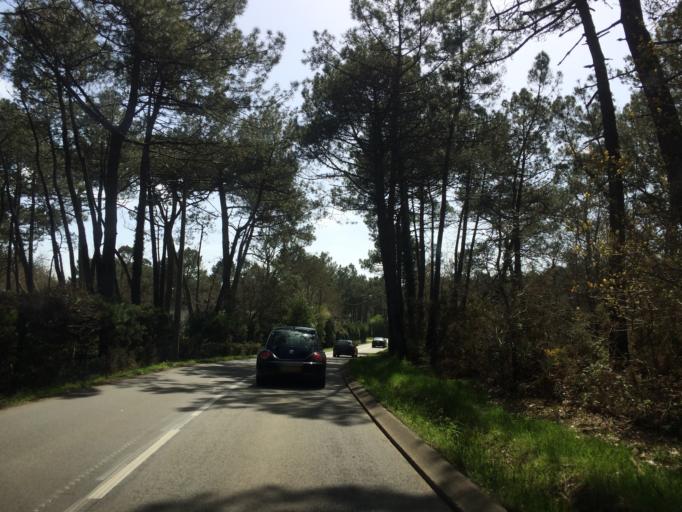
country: FR
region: Brittany
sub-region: Departement du Morbihan
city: Ploemel
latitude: 47.6283
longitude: -3.0494
